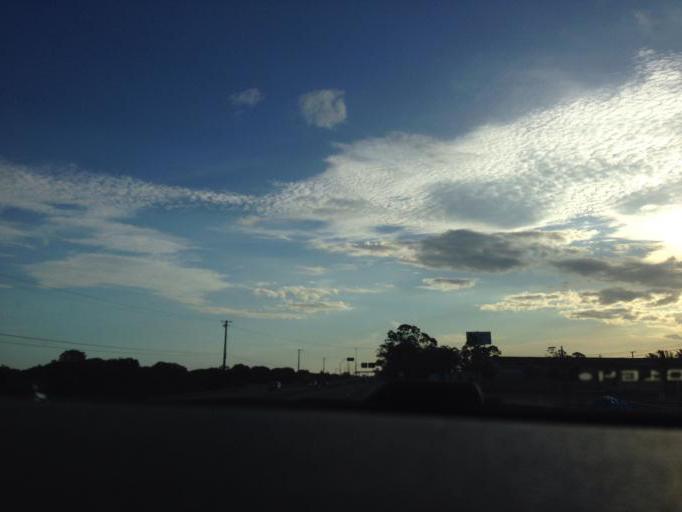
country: BR
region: Espirito Santo
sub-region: Guarapari
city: Guarapari
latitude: -20.5365
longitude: -40.3884
